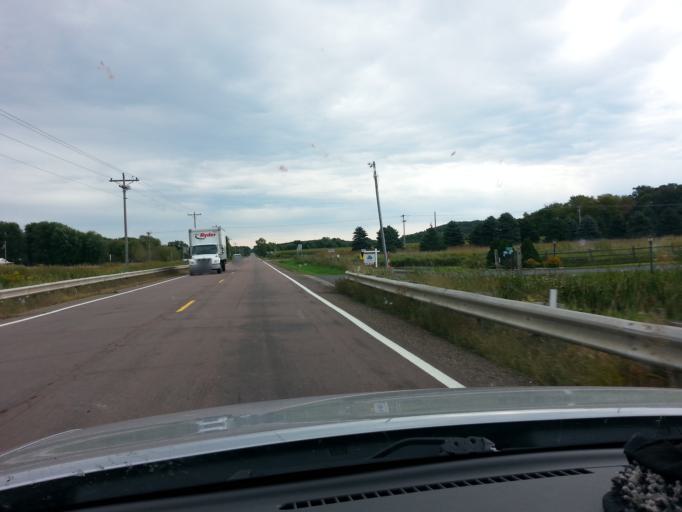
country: US
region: Minnesota
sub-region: Dakota County
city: Farmington
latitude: 44.6303
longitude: -93.0574
